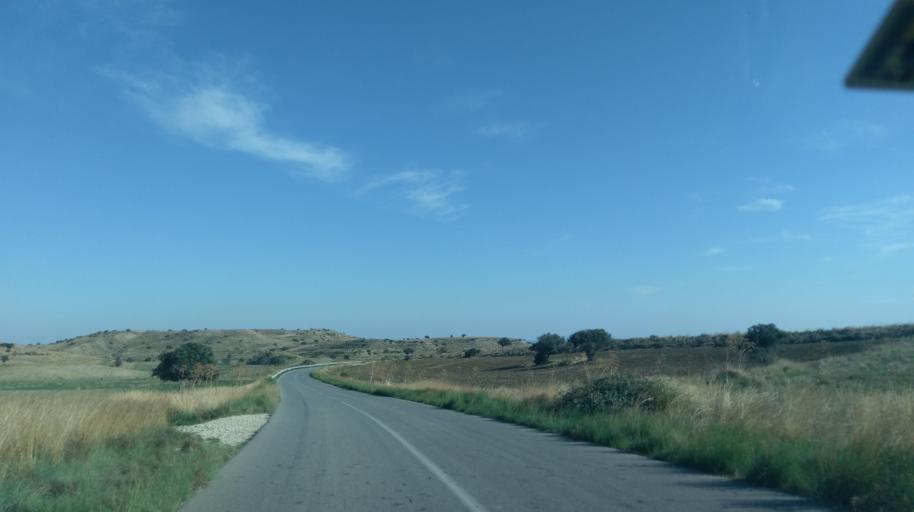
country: CY
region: Ammochostos
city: Trikomo
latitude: 35.3048
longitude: 33.8427
